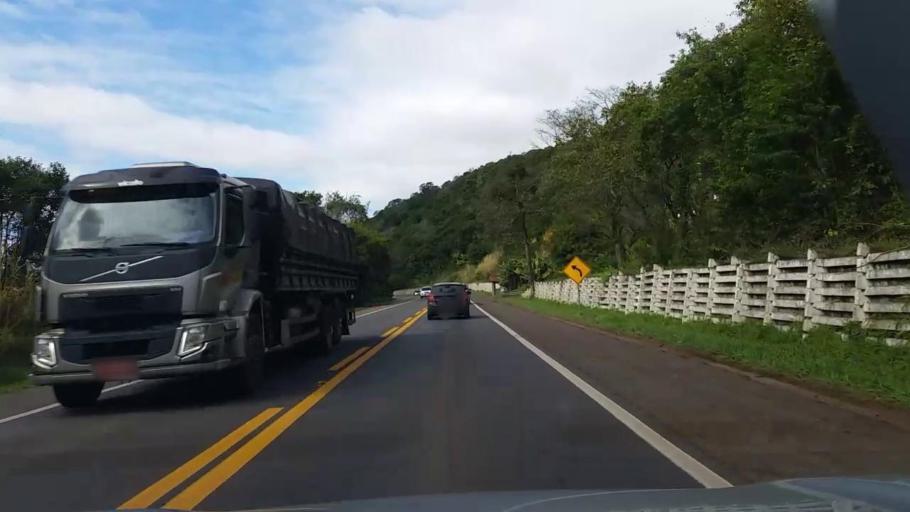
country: BR
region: Rio Grande do Sul
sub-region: Arroio Do Meio
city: Arroio do Meio
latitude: -29.3346
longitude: -52.0956
